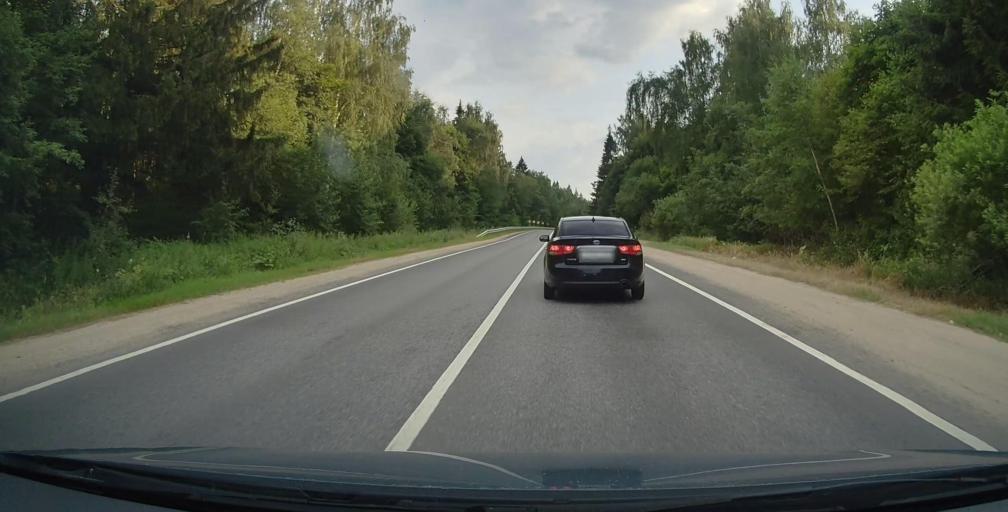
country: RU
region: Moskovskaya
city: Shemetovo
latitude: 56.4934
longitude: 38.1012
